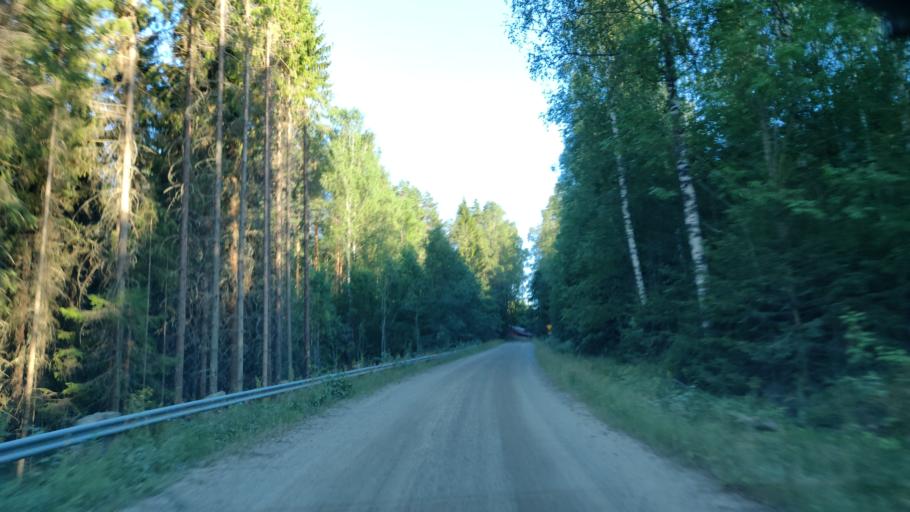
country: SE
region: Vaermland
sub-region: Hagfors Kommun
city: Ekshaerad
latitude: 60.1588
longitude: 13.5140
